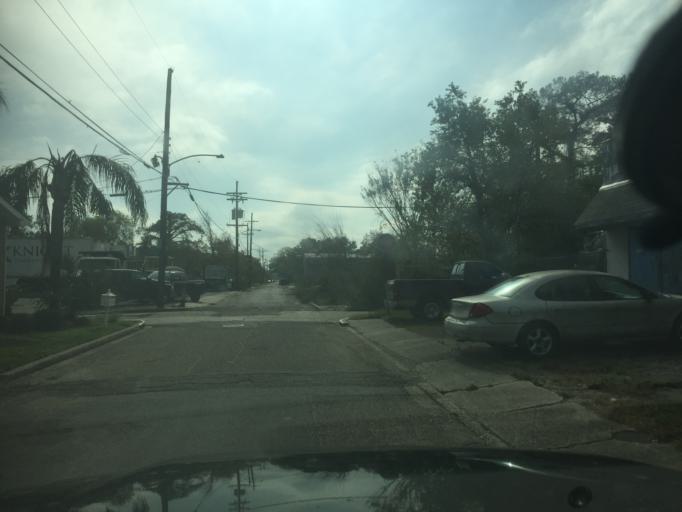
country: US
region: Louisiana
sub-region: Saint Bernard Parish
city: Arabi
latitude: 30.0013
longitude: -90.0361
